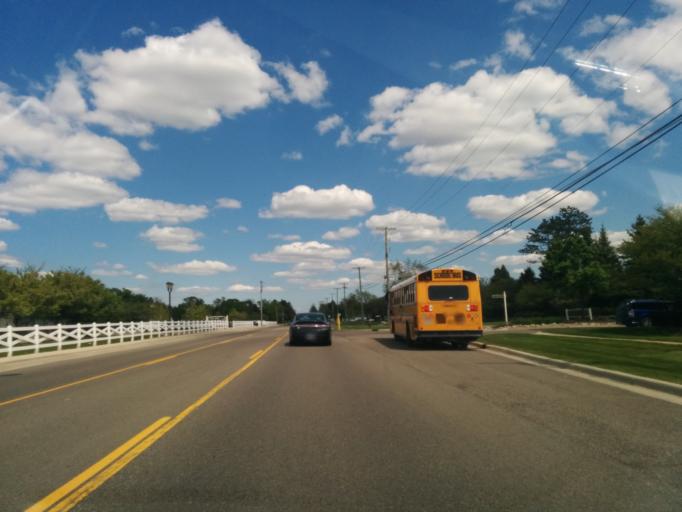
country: US
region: Michigan
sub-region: Oakland County
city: Farmington Hills
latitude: 42.5138
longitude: -83.3550
